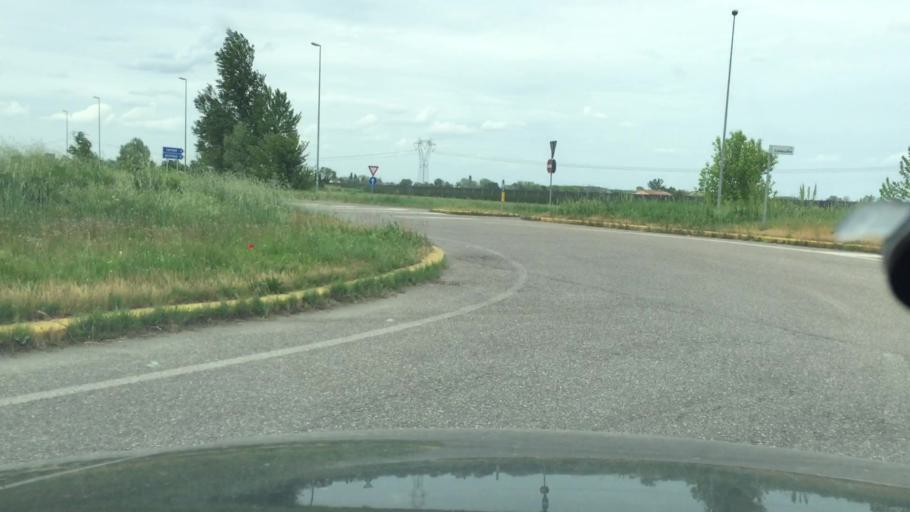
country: IT
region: Emilia-Romagna
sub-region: Provincia di Ferrara
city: Cona
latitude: 44.8048
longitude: 11.7202
